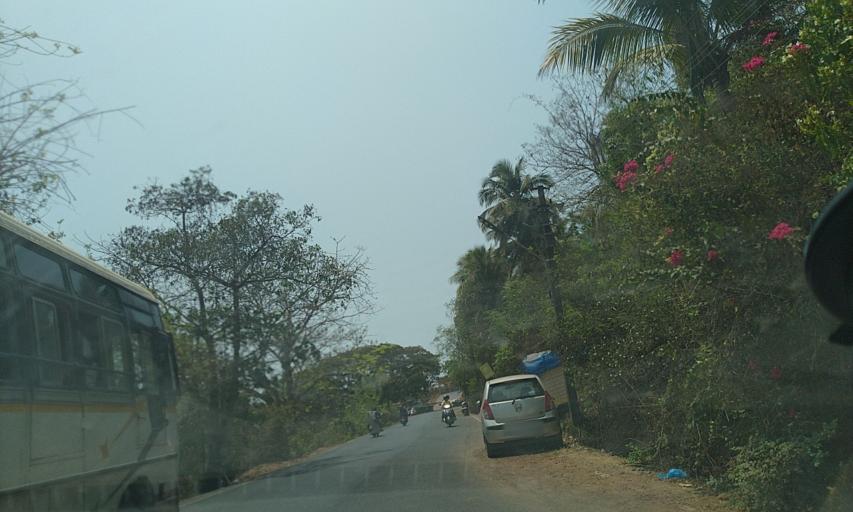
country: IN
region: Goa
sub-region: North Goa
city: Mapuca
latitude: 15.5958
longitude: 73.7988
